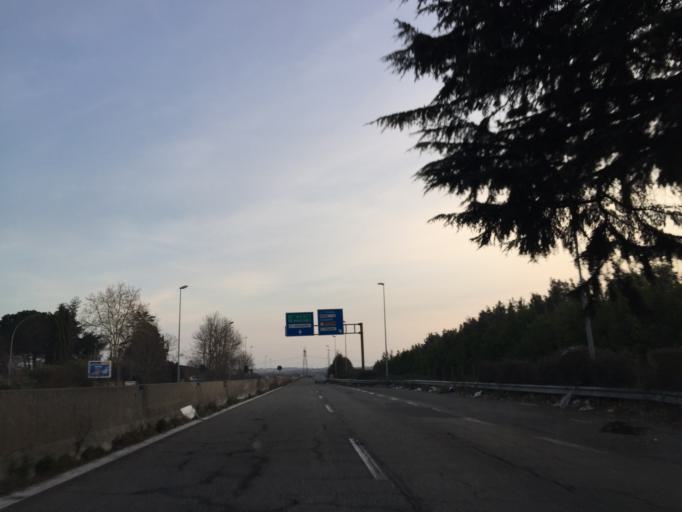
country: IT
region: Latium
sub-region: Citta metropolitana di Roma Capitale
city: Le Rughe
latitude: 42.0602
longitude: 12.3729
